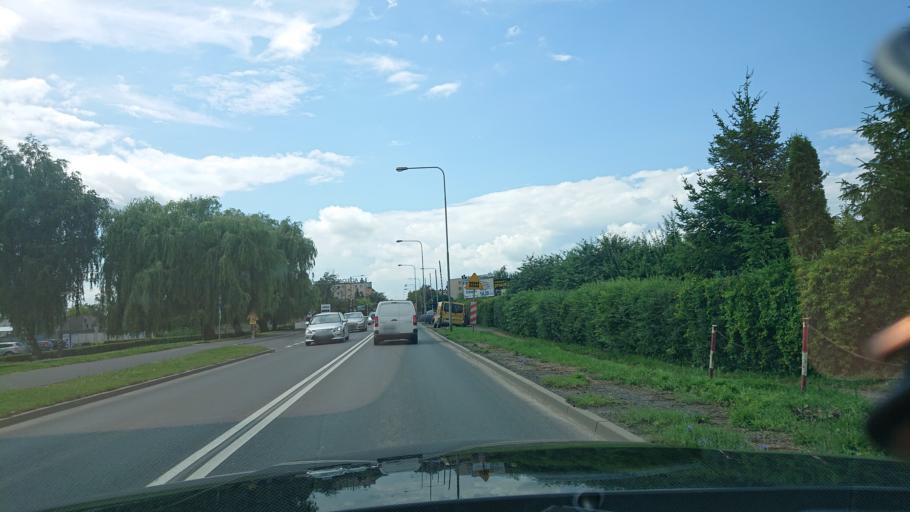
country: PL
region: Greater Poland Voivodeship
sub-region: Powiat gnieznienski
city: Gniezno
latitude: 52.5414
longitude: 17.6277
